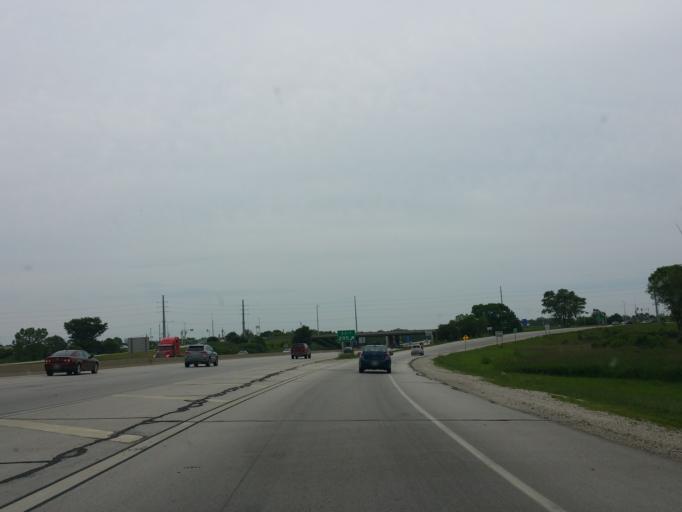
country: US
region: Wisconsin
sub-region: Waukesha County
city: Waukesha
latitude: 43.0487
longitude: -88.2118
